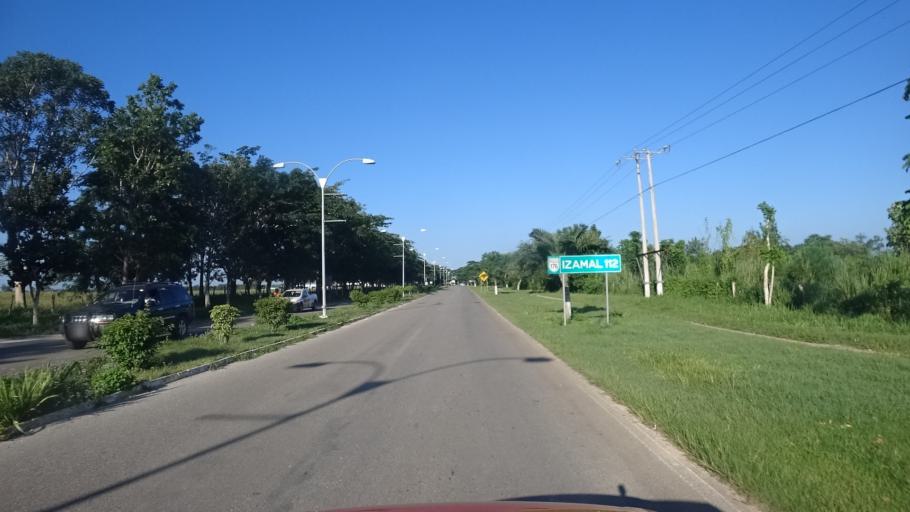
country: MX
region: Yucatan
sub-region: Tizimin
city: Tizimin
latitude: 21.1520
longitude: -88.1753
